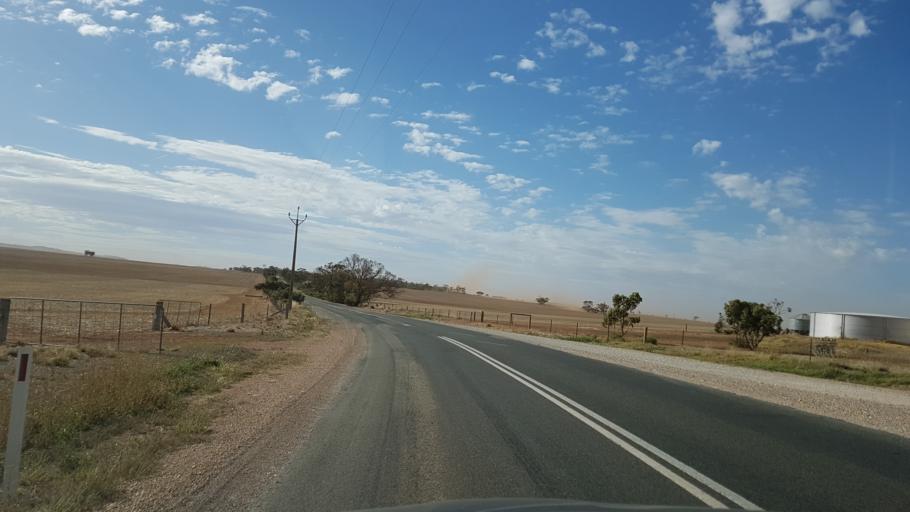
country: AU
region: South Australia
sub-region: Clare and Gilbert Valleys
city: Clare
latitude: -33.9824
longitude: 138.5046
